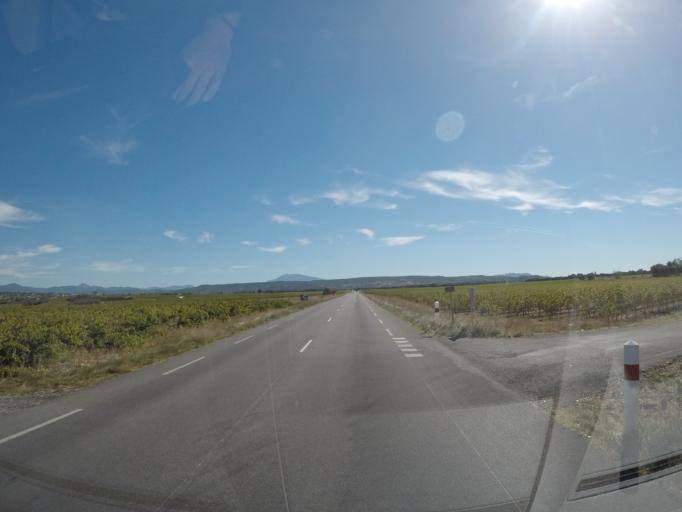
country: FR
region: Provence-Alpes-Cote d'Azur
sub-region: Departement du Vaucluse
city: Sainte-Cecile-les-Vignes
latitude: 44.2816
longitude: 4.8906
